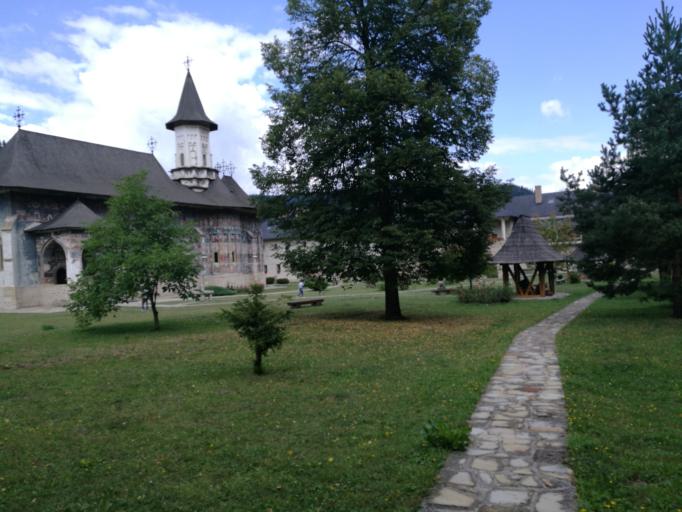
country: RO
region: Suceava
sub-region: Comuna Sucevita
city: Sucevita
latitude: 47.7775
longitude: 25.7109
